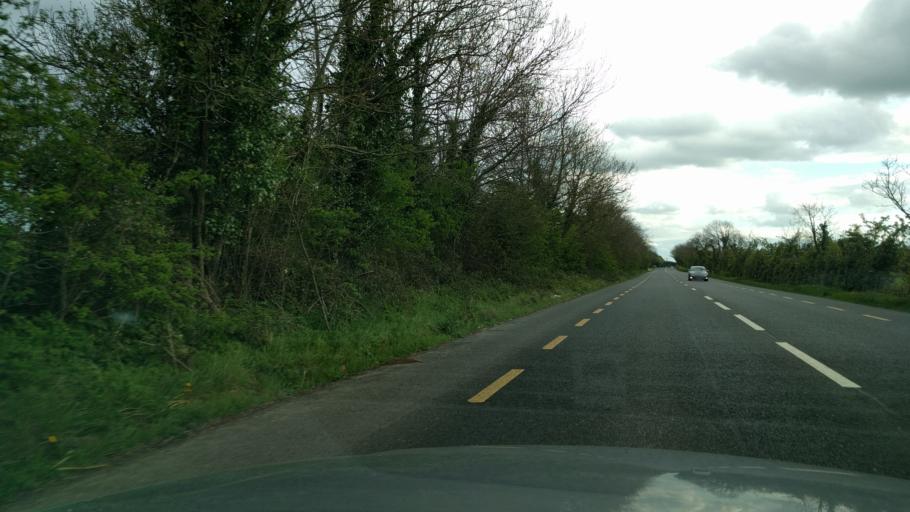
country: IE
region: Leinster
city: Balrothery
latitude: 53.5803
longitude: -6.1988
